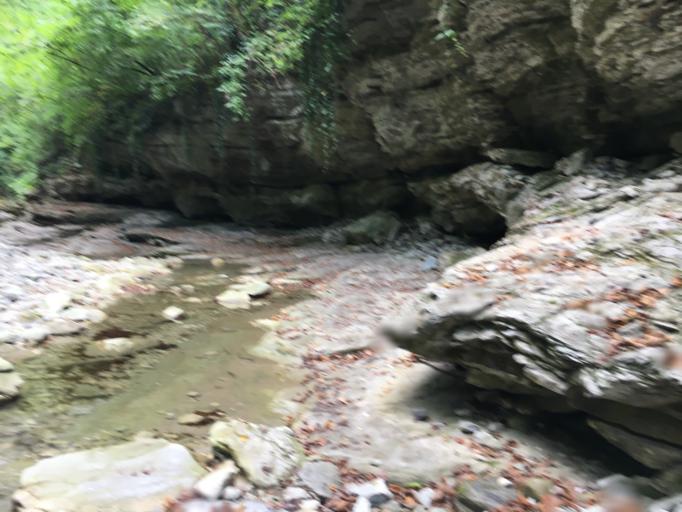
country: RU
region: Krasnodarskiy
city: Tuapse
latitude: 44.2628
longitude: 39.2058
